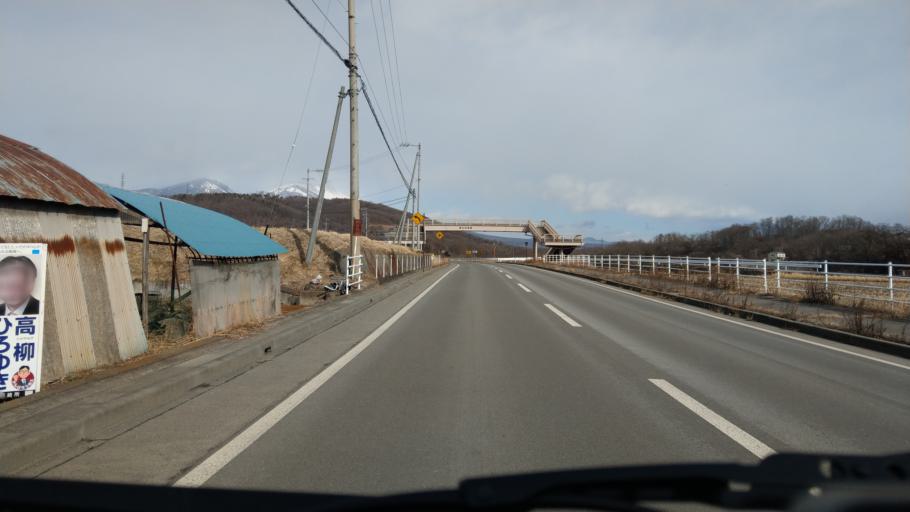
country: JP
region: Nagano
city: Komoro
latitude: 36.2789
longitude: 138.3991
